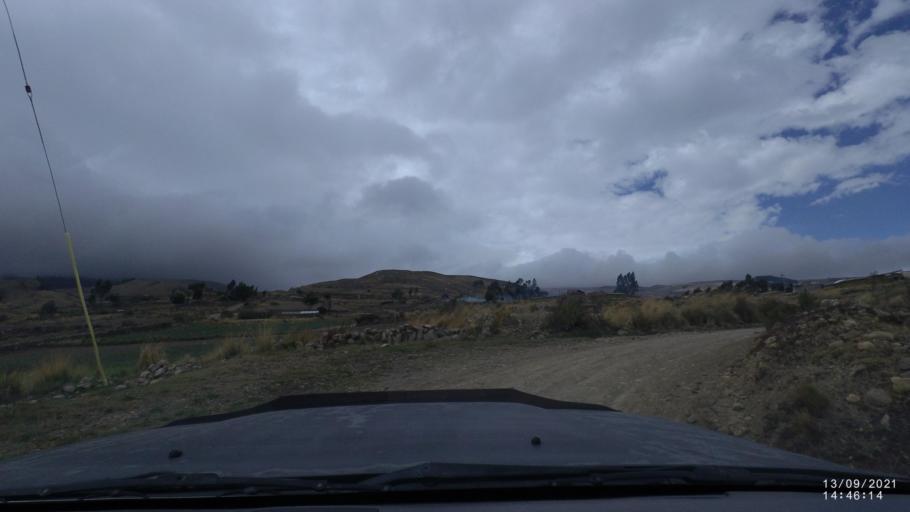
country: BO
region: Cochabamba
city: Colomi
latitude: -17.3510
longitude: -65.8050
